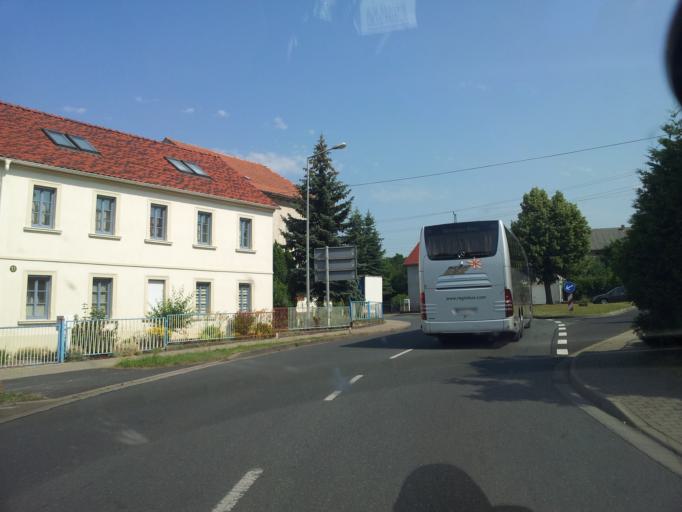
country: DE
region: Saxony
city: Stauchitz
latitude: 51.2443
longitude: 13.2115
